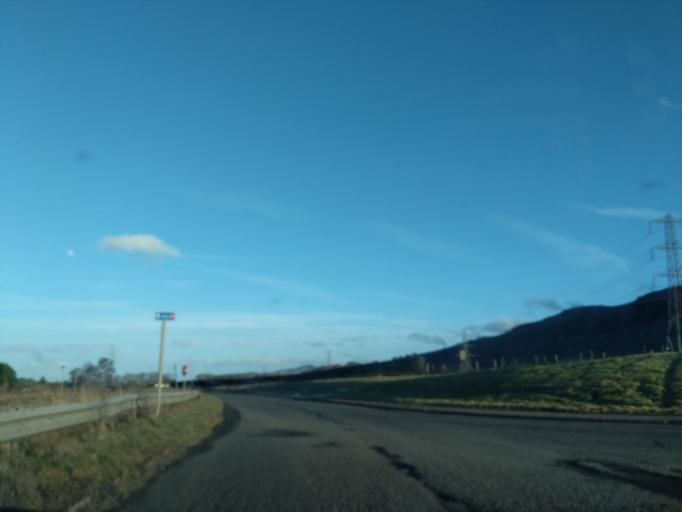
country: GB
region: Scotland
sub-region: Edinburgh
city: Ratho
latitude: 55.8920
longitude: -3.3883
